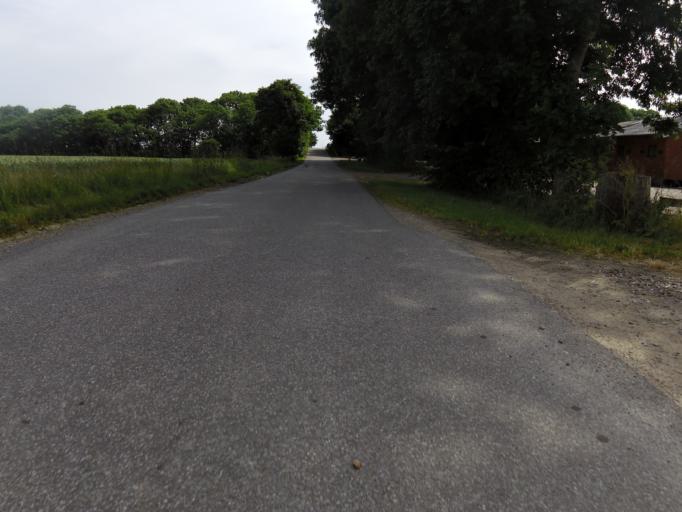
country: DK
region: Central Jutland
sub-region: Holstebro Kommune
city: Holstebro
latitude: 56.4280
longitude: 8.6426
